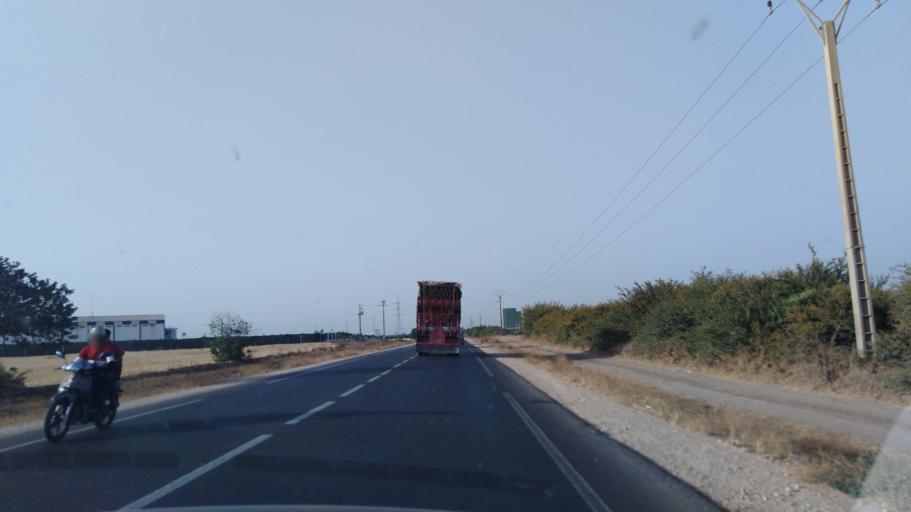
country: MA
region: Chaouia-Ouardigha
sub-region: Settat Province
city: Berrechid
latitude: 33.1397
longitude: -7.6243
